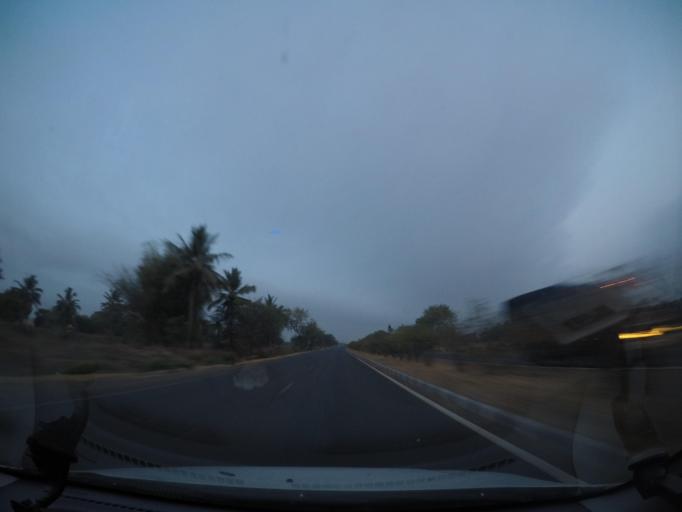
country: IN
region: Andhra Pradesh
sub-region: West Godavari
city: Tadepallegudem
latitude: 16.8164
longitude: 81.3843
